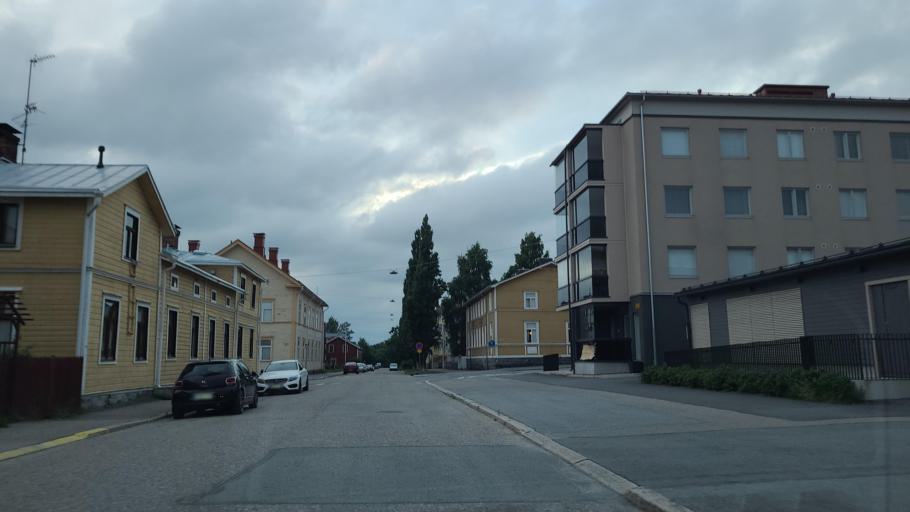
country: FI
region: Ostrobothnia
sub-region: Vaasa
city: Vaasa
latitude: 63.1014
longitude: 21.6176
